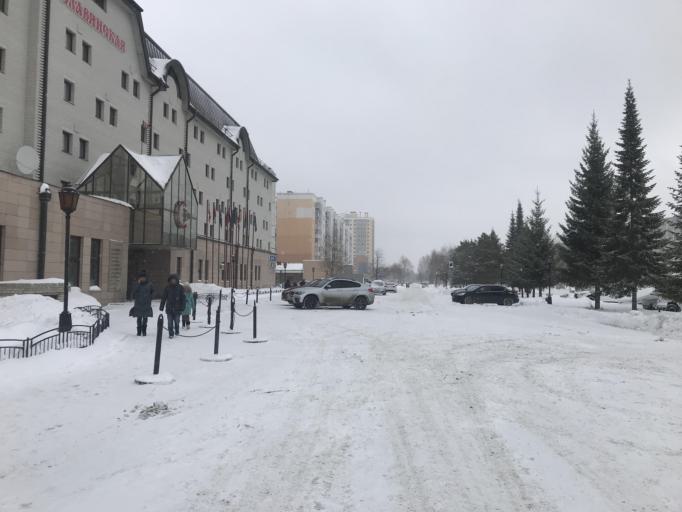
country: RU
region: Tjumen
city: Tobol'sk
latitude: 58.2283
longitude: 68.2780
